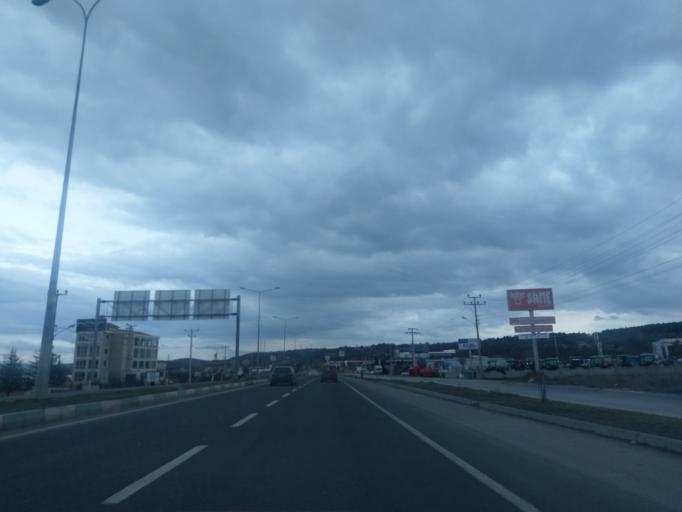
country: TR
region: Kuetahya
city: Kutahya
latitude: 39.3825
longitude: 30.0450
